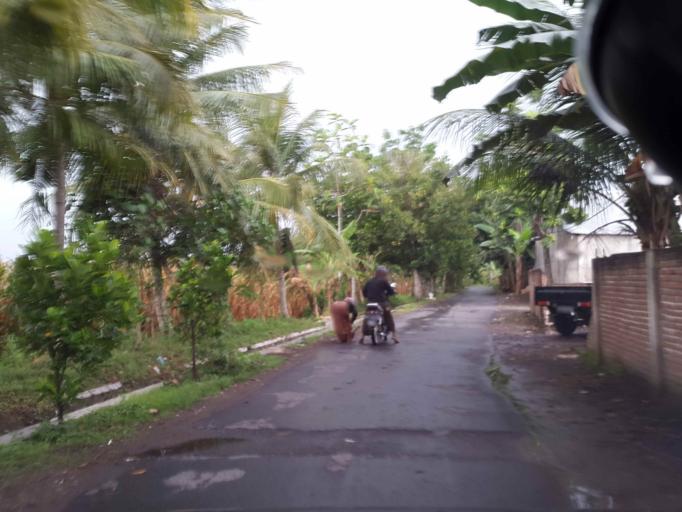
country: ID
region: West Nusa Tenggara
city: Karangkebon Timur
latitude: -8.6703
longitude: 116.1185
